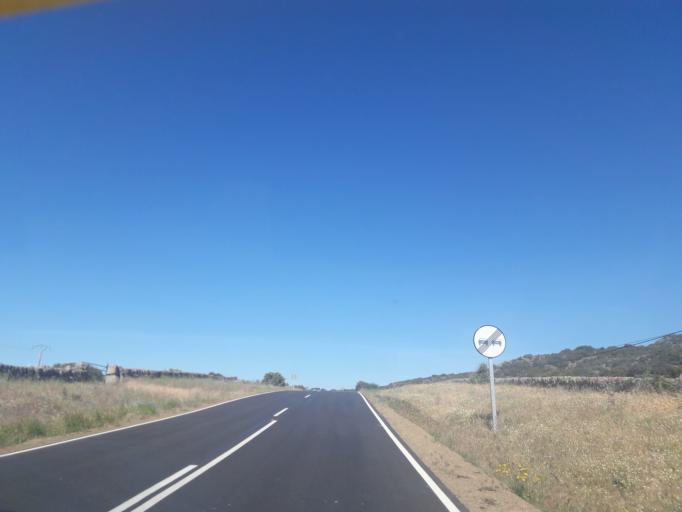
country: ES
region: Castille and Leon
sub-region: Provincia de Salamanca
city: Santibanez de Bejar
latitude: 40.4817
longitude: -5.6230
